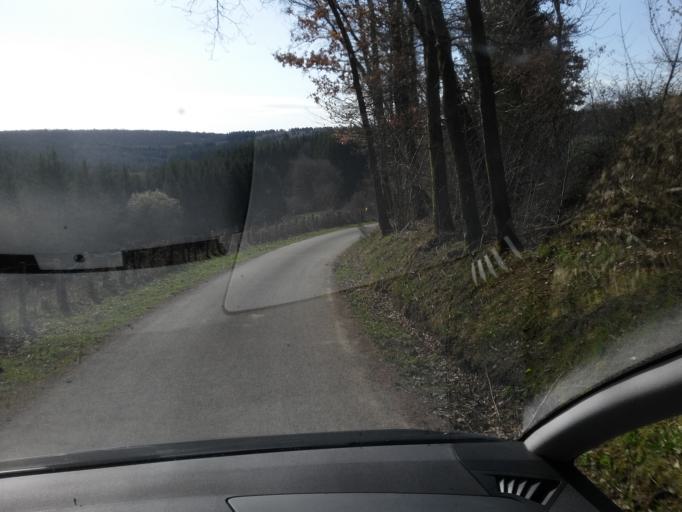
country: BE
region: Wallonia
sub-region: Province du Luxembourg
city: Daverdisse
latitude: 49.9945
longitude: 5.1487
